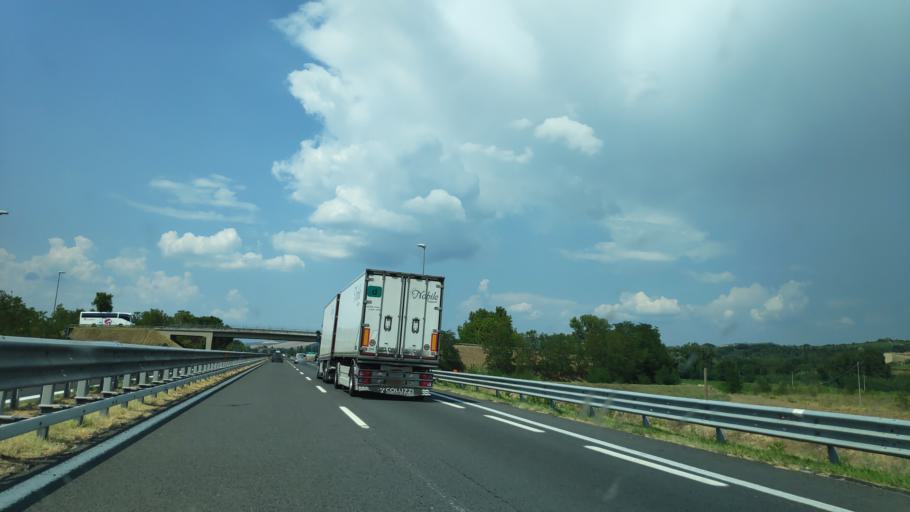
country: IT
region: Umbria
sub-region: Provincia di Terni
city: Orvieto Scalo
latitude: 42.7126
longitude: 12.1523
